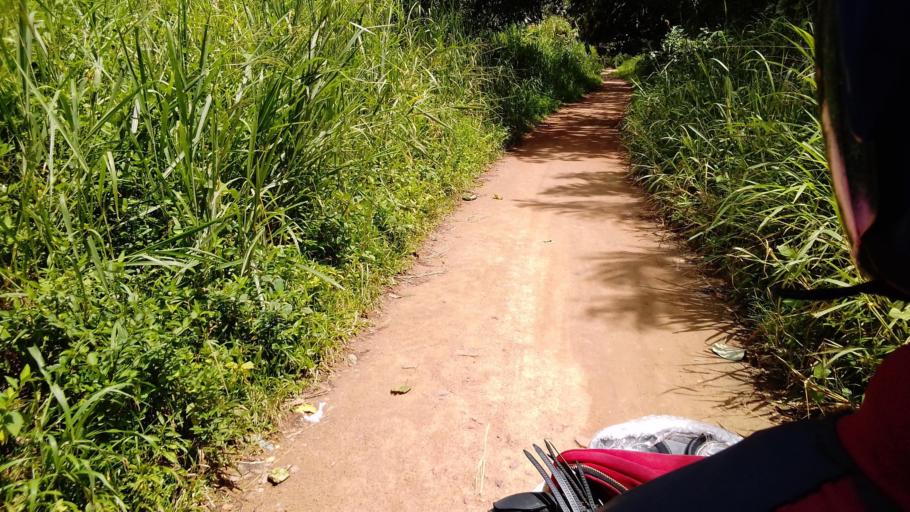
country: SL
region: Eastern Province
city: Koidu
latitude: 8.6776
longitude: -10.9876
